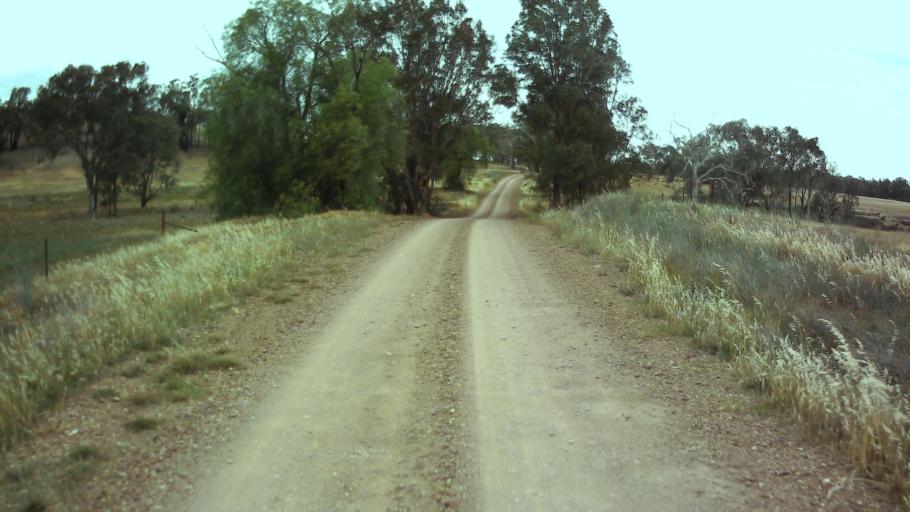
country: AU
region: New South Wales
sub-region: Weddin
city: Grenfell
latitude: -33.9115
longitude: 148.2903
